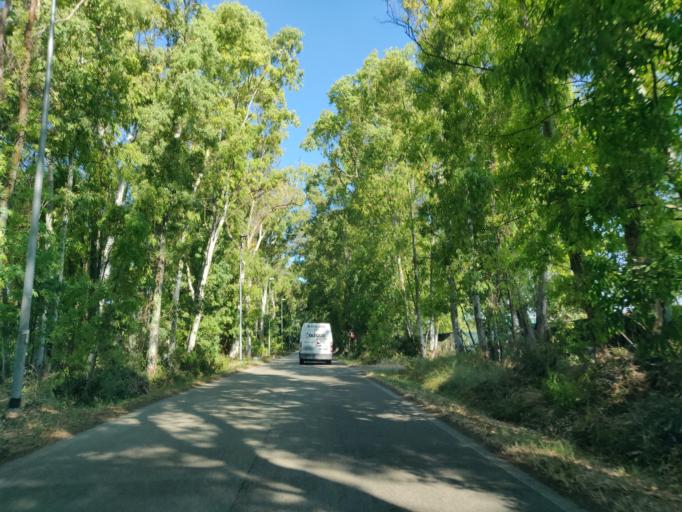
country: IT
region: Latium
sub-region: Citta metropolitana di Roma Capitale
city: Aurelia
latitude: 42.1601
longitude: 11.7488
